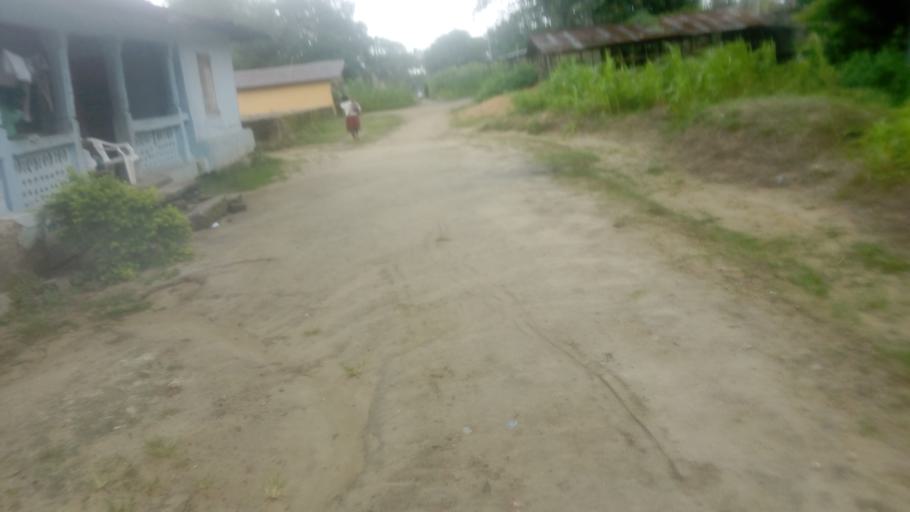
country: SL
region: Northern Province
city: Lunsar
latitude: 8.6825
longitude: -12.5381
